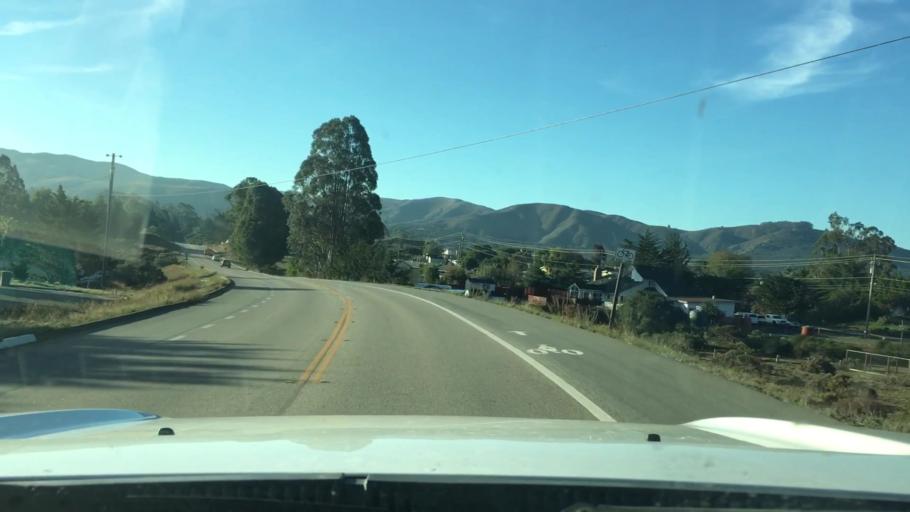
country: US
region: California
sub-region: San Luis Obispo County
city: Los Osos
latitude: 35.3205
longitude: -120.8233
